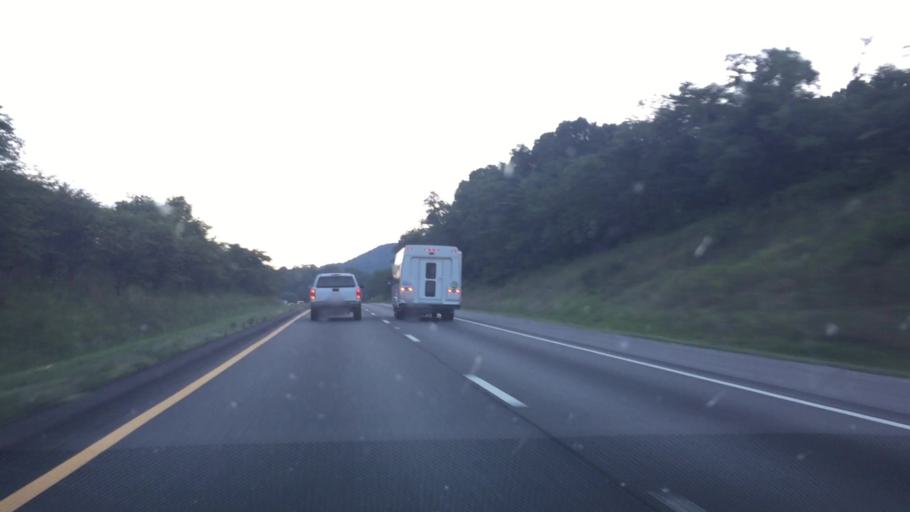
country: US
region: Virginia
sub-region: Montgomery County
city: Shawsville
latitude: 37.2504
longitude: -80.1986
